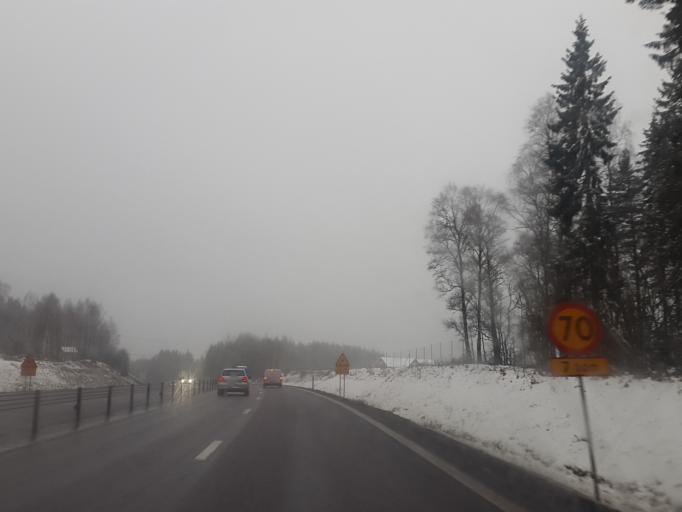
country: SE
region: Joenkoeping
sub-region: Jonkopings Kommun
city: Jonkoping
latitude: 57.7571
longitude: 14.1070
